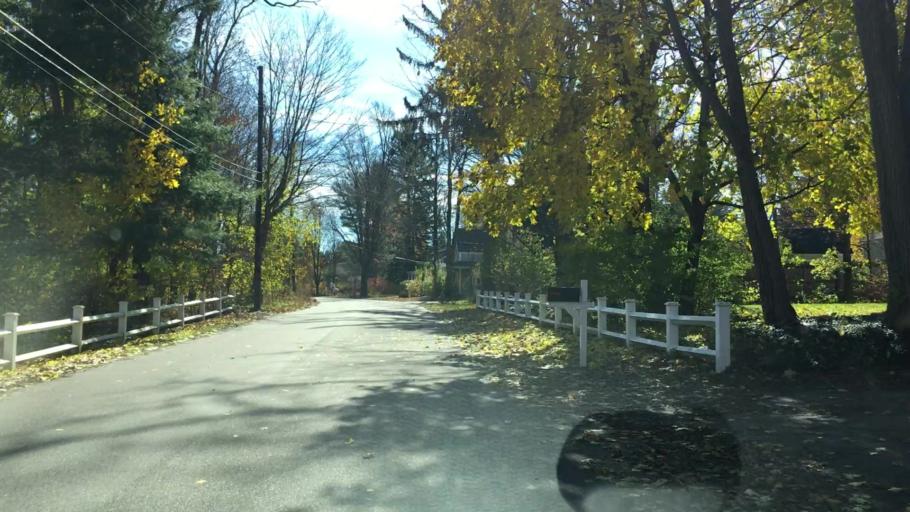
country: US
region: New Hampshire
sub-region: Hillsborough County
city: Milford
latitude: 42.8633
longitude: -71.6238
